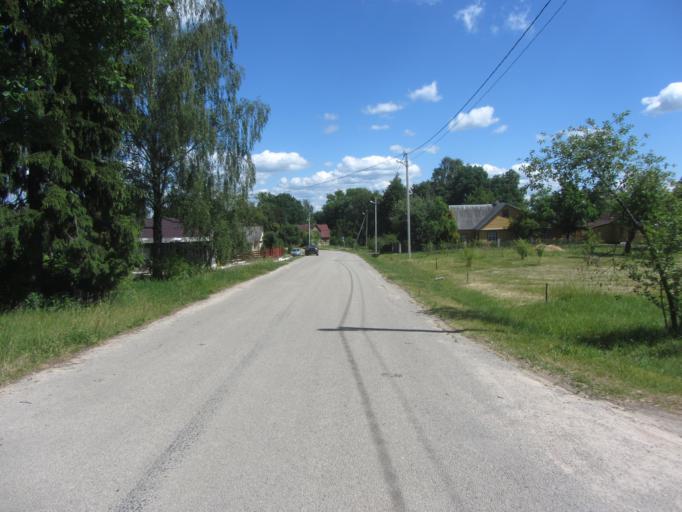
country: LT
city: Jieznas
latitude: 54.7891
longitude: 24.1784
